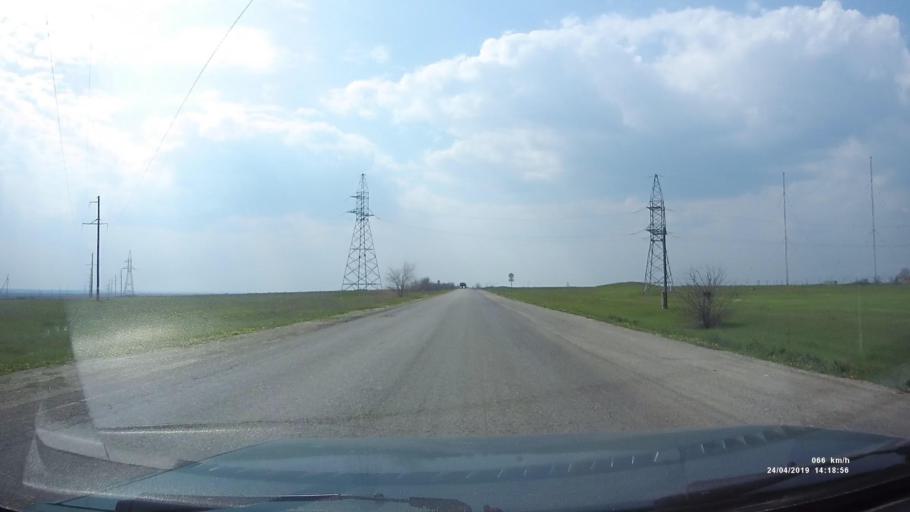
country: RU
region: Kalmykiya
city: Arshan'
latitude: 46.3040
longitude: 44.1843
